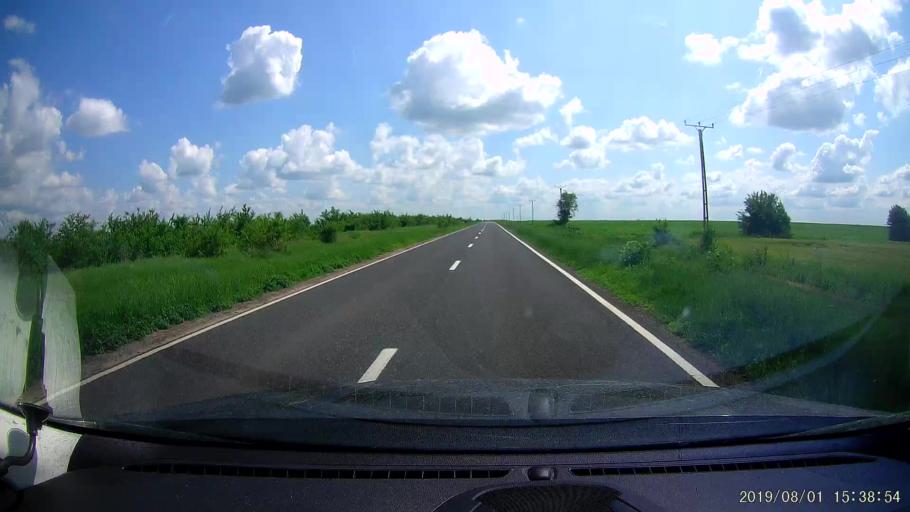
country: RO
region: Braila
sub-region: Comuna Insuratei
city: Insuratei
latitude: 44.8706
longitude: 27.5693
